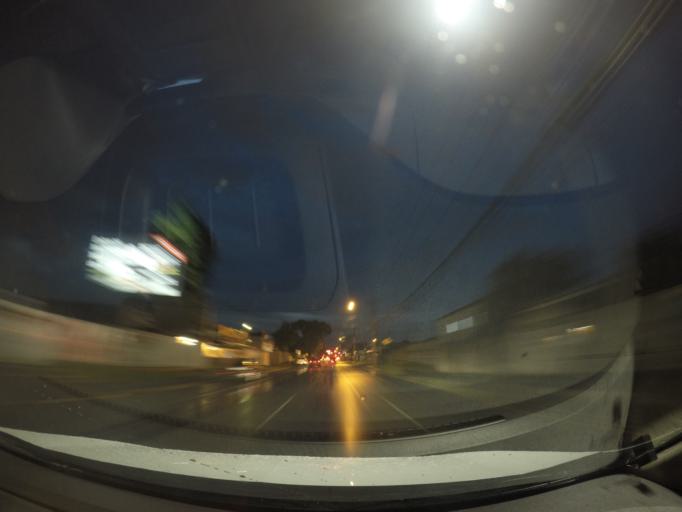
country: BR
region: Parana
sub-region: Curitiba
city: Curitiba
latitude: -25.4773
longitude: -49.2562
